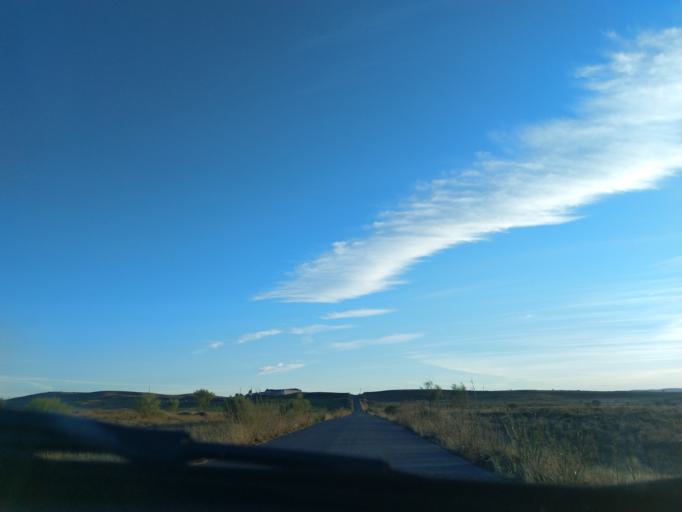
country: ES
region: Extremadura
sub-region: Provincia de Badajoz
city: Berlanga
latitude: 38.2667
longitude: -5.8238
